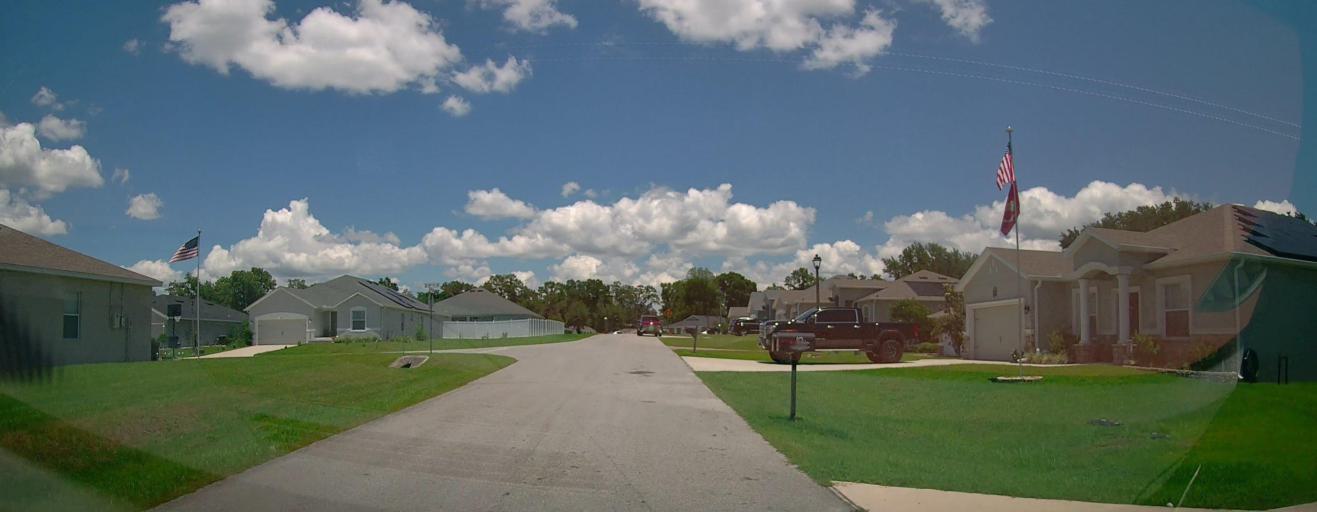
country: US
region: Florida
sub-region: Marion County
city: Belleview
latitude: 29.0917
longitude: -82.0635
